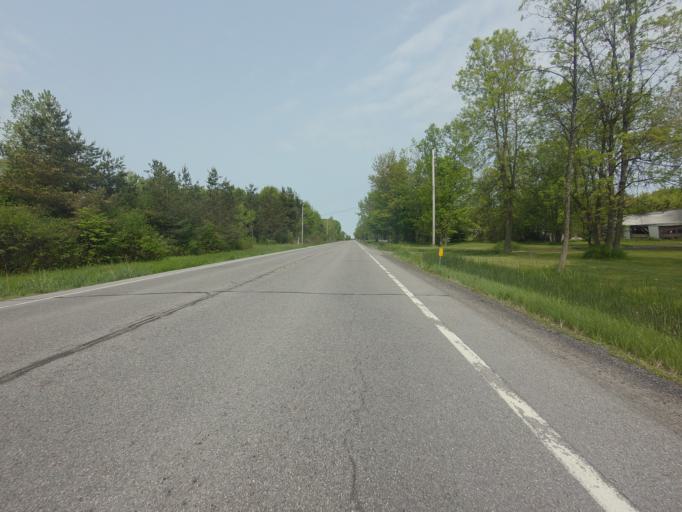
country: US
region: New York
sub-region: Jefferson County
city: Dexter
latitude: 44.0177
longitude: -76.0274
